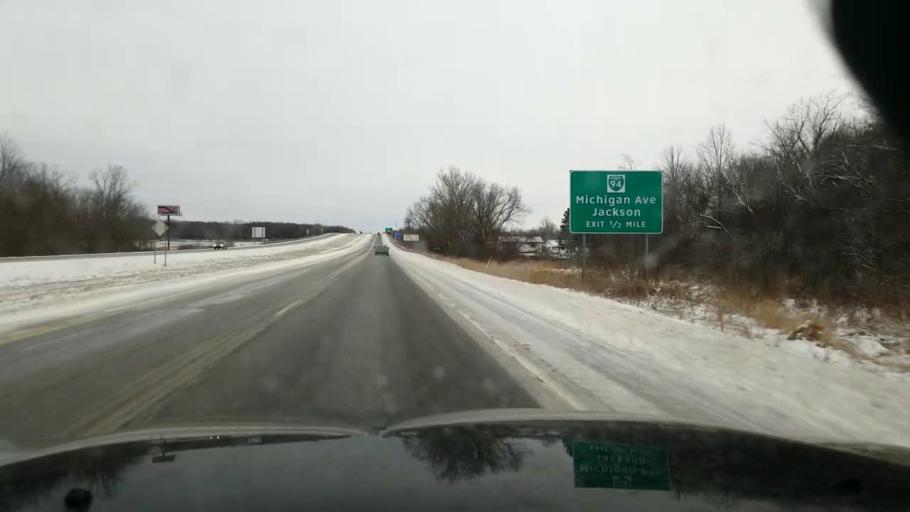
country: US
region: Michigan
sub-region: Jackson County
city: Jackson
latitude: 42.2612
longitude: -84.4768
